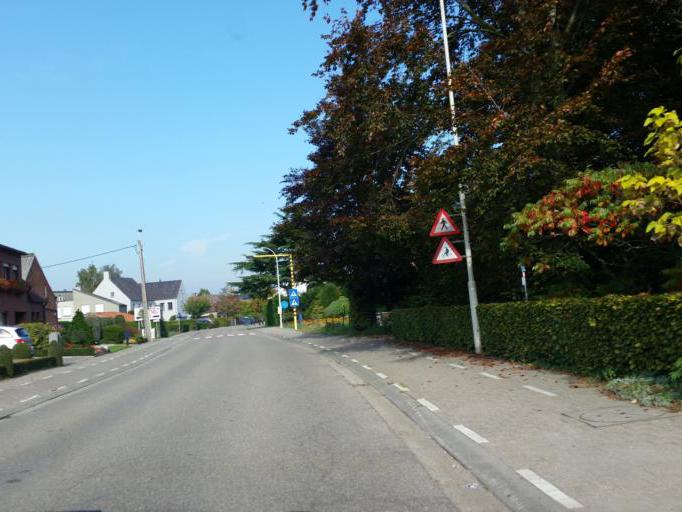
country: BE
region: Flanders
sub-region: Provincie Antwerpen
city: Aartselaar
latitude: 51.1281
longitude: 4.4019
